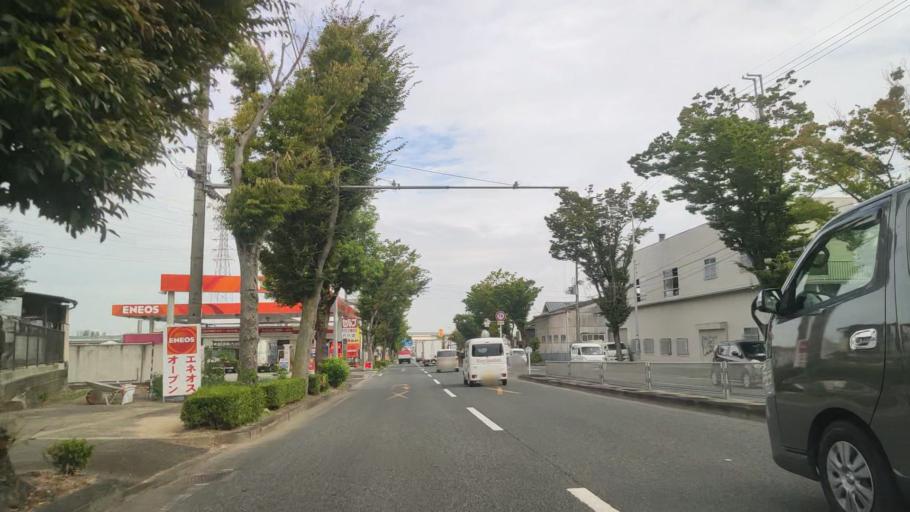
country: JP
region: Osaka
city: Tondabayashicho
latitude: 34.5283
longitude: 135.6049
